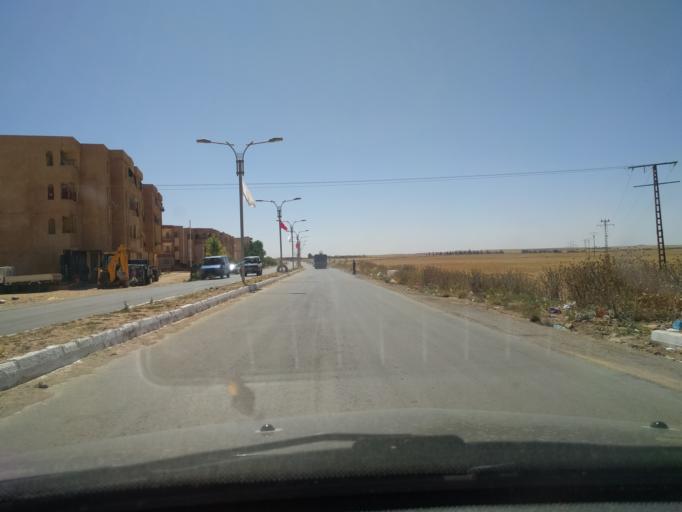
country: DZ
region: Tiaret
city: Frenda
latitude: 34.9039
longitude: 1.1124
